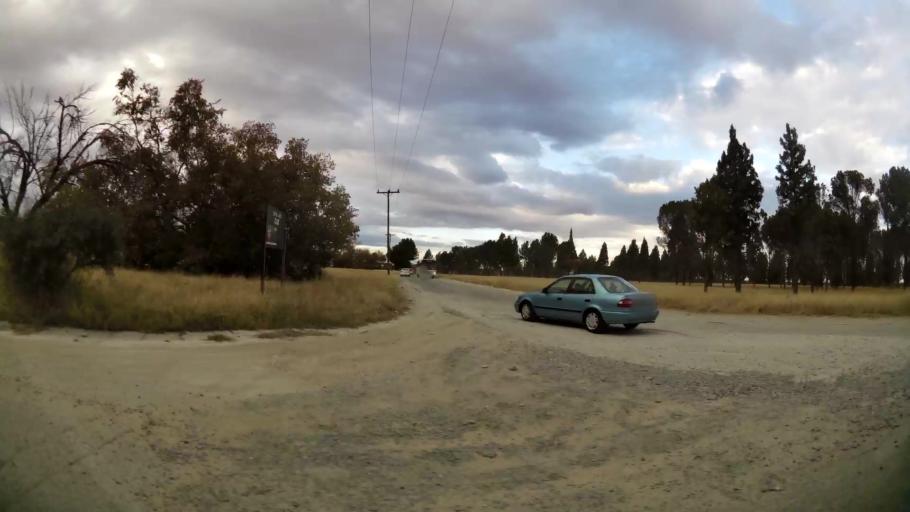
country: ZA
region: Orange Free State
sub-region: Lejweleputswa District Municipality
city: Welkom
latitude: -27.9702
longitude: 26.7009
